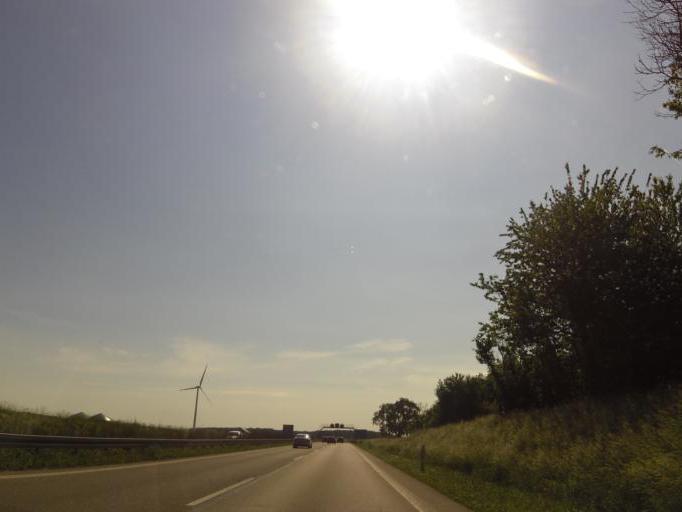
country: DE
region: Baden-Wuerttemberg
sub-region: Tuebingen Region
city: Bernstadt
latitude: 48.4556
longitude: 10.0315
